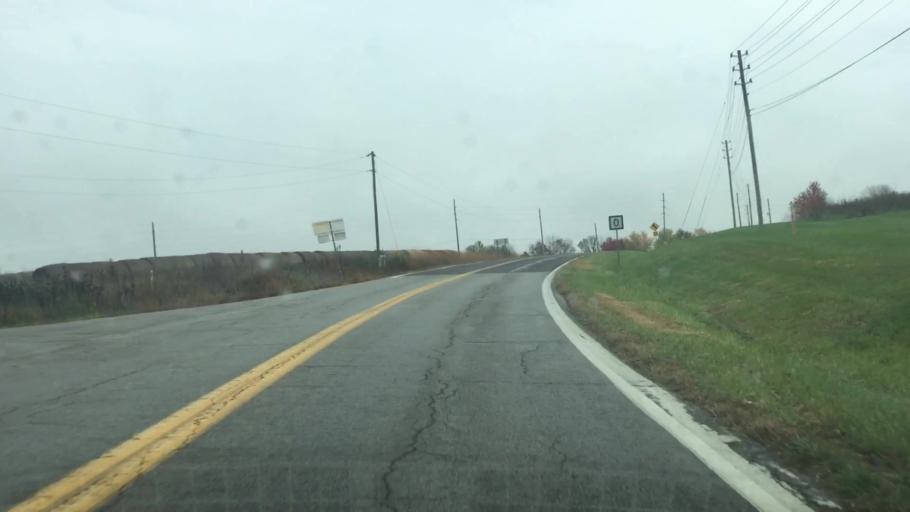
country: US
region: Missouri
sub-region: Callaway County
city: Fulton
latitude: 38.8404
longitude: -91.9237
